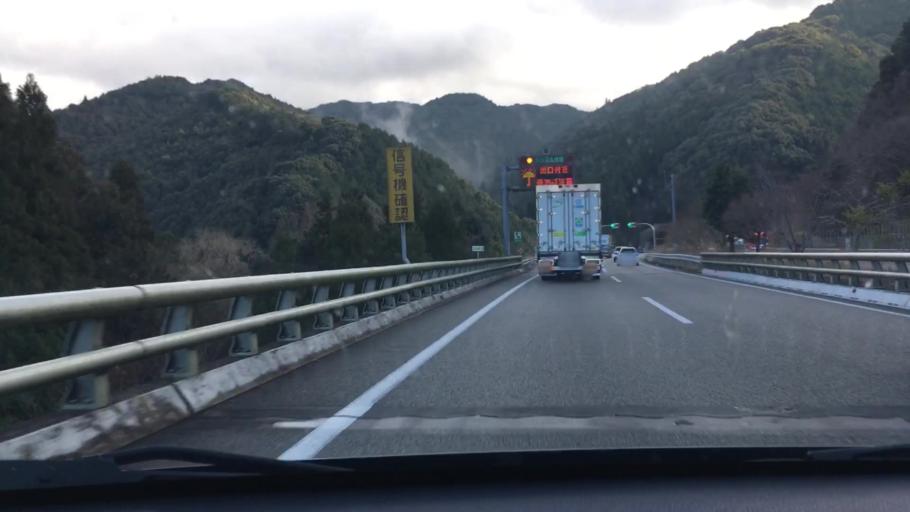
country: JP
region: Kumamoto
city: Hitoyoshi
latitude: 32.1366
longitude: 130.8032
